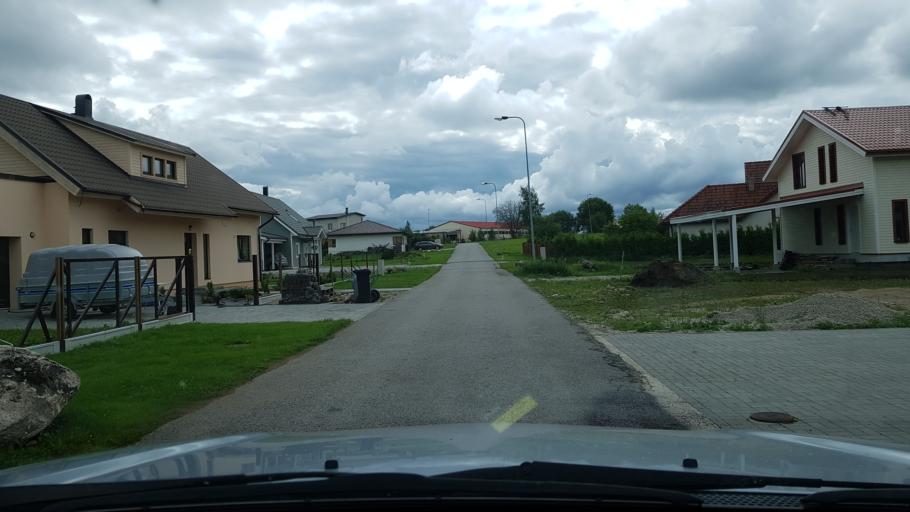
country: EE
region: Harju
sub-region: Rae vald
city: Vaida
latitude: 59.3190
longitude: 24.9445
